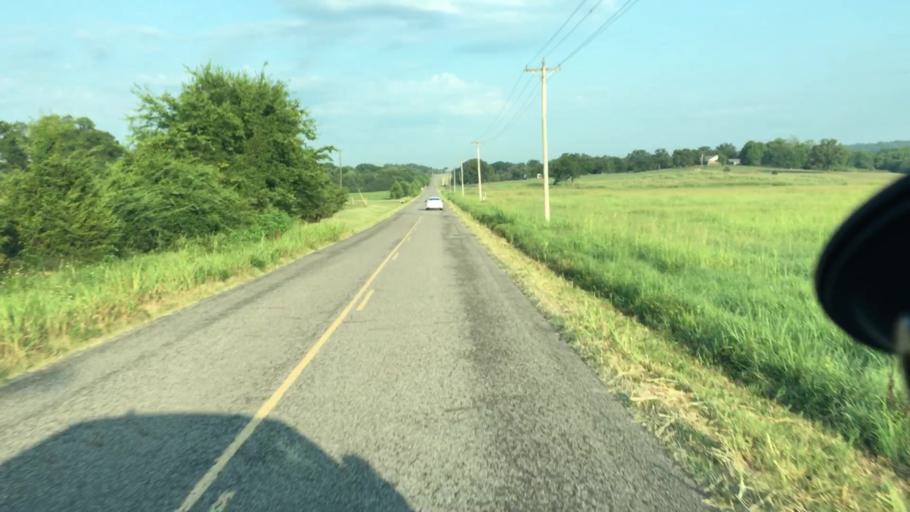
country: US
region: Arkansas
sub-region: Johnson County
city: Coal Hill
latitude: 35.3663
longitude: -93.6022
